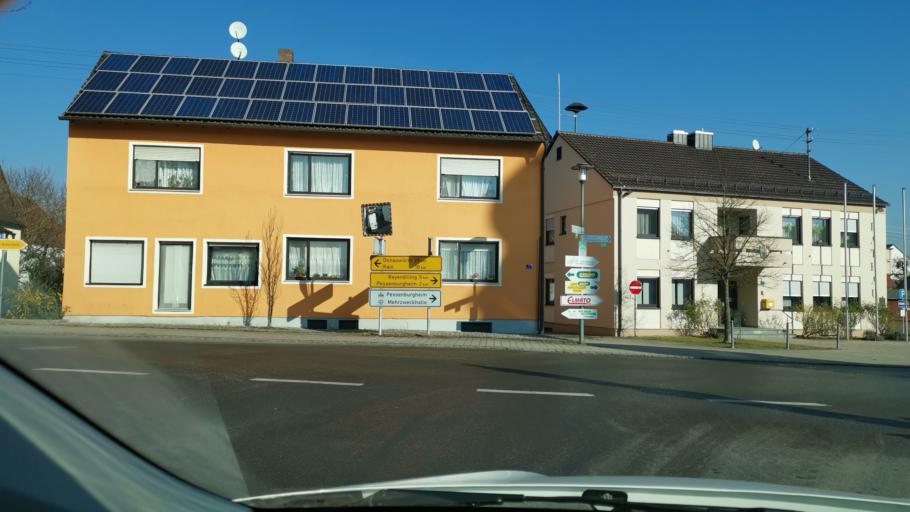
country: DE
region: Bavaria
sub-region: Swabia
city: Holzheim
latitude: 48.6127
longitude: 10.9500
